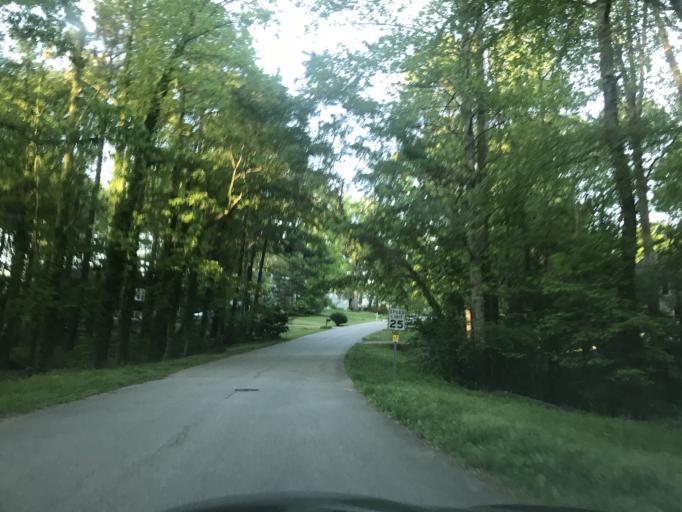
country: US
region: North Carolina
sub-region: Wake County
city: Wake Forest
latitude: 35.8995
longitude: -78.6034
